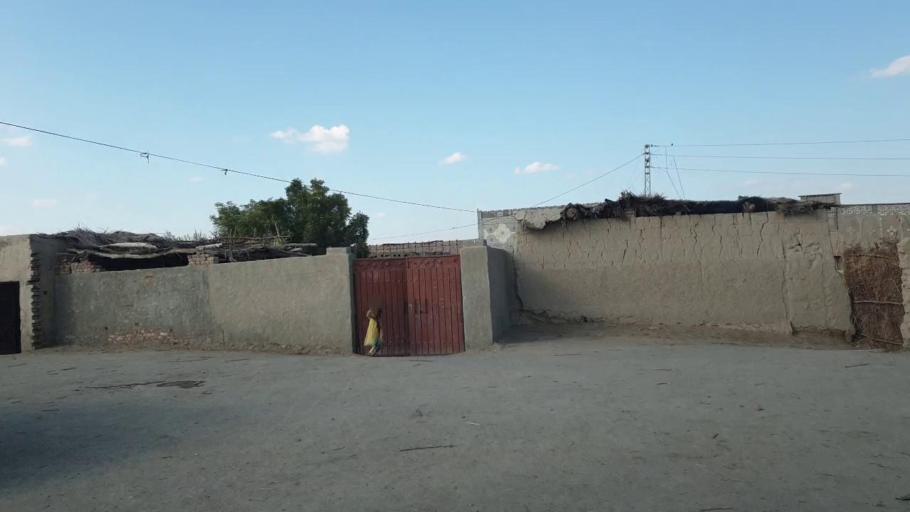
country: PK
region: Sindh
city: Shahpur Chakar
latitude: 26.1045
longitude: 68.5896
